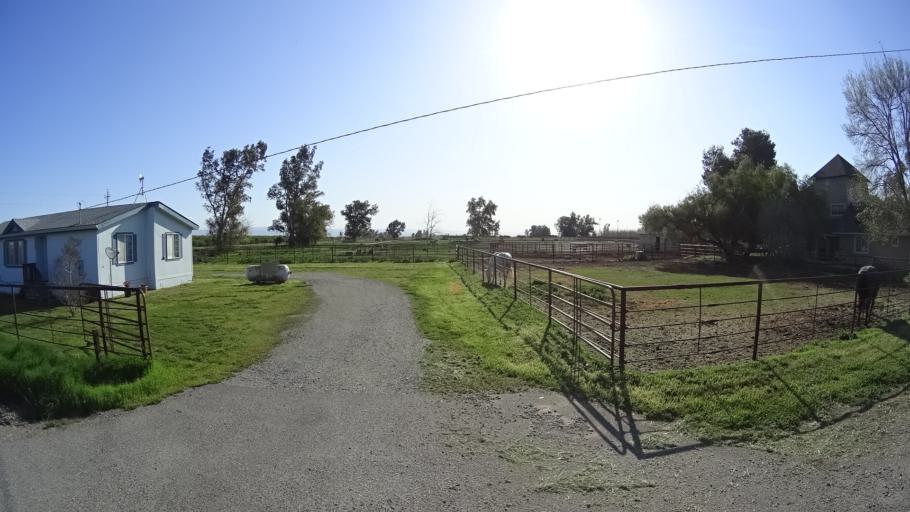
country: US
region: California
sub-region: Glenn County
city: Orland
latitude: 39.7679
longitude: -122.1321
